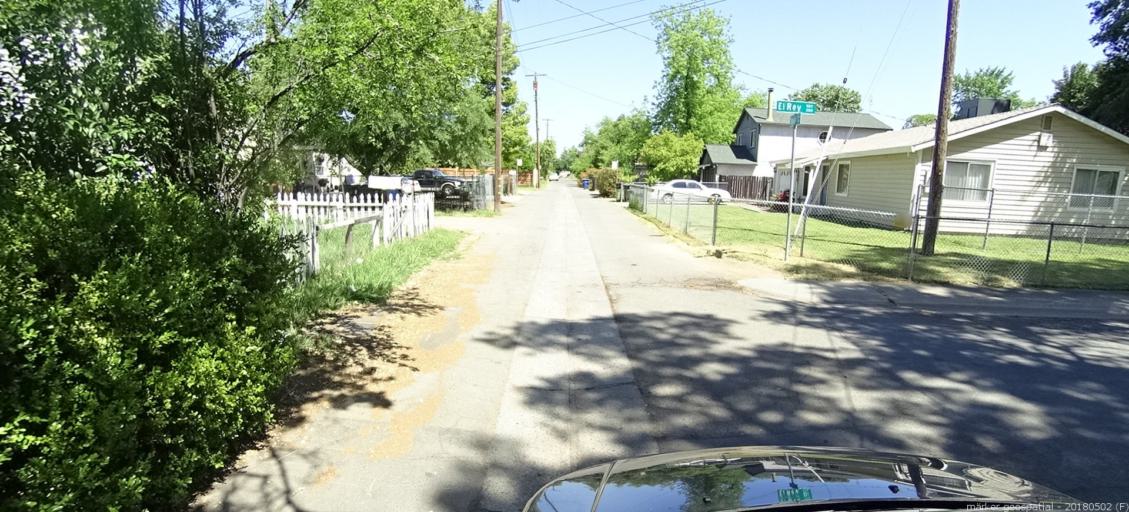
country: US
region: California
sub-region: Sacramento County
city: Arden-Arcade
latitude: 38.6253
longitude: -121.4405
